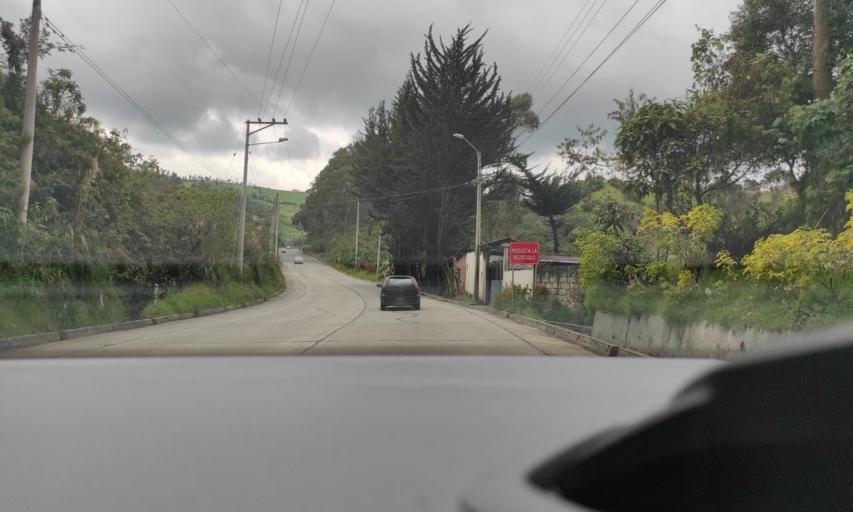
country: EC
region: Canar
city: Azogues
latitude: -2.6693
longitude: -78.8976
